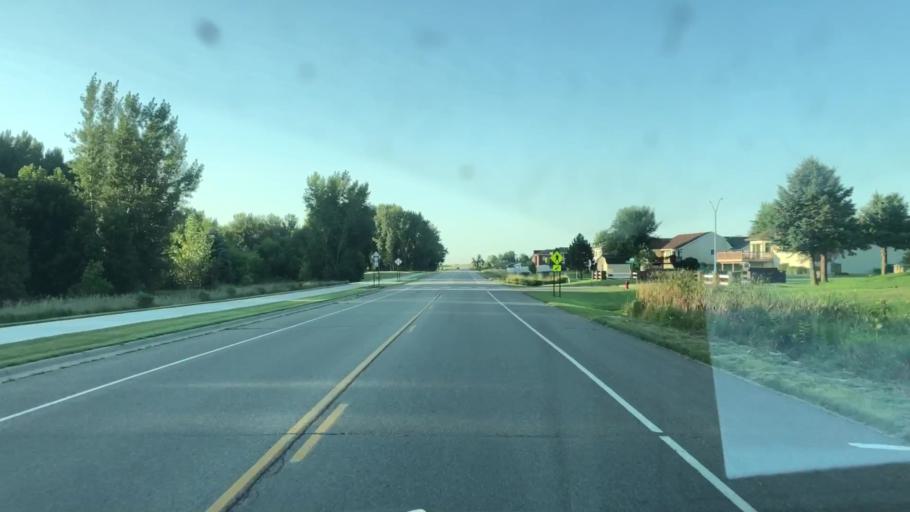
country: US
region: Minnesota
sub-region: Nobles County
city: Worthington
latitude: 43.6131
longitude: -95.6367
